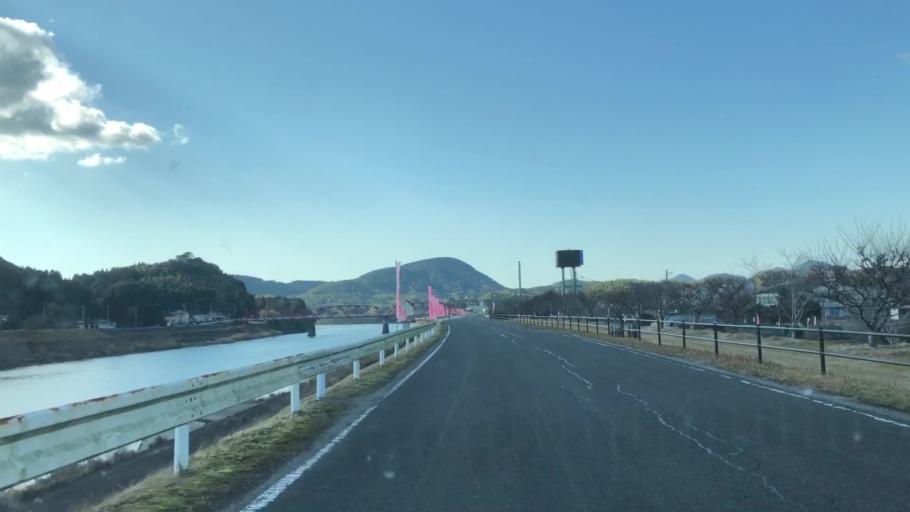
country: JP
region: Kagoshima
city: Satsumasendai
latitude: 31.8608
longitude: 130.3426
